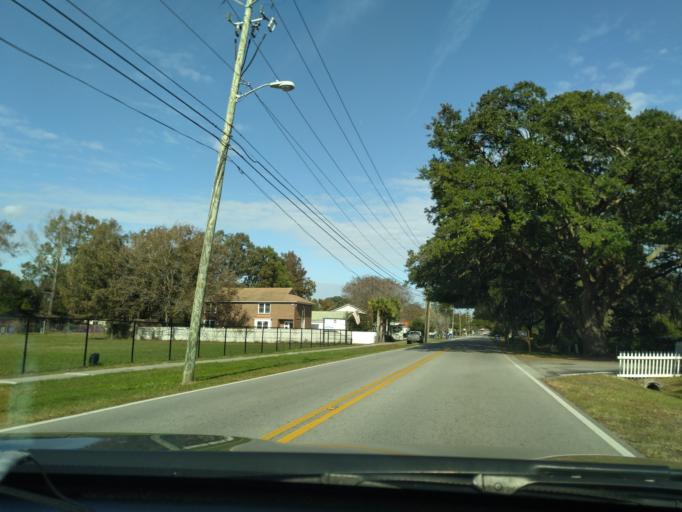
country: US
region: South Carolina
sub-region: Charleston County
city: North Charleston
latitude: 32.7916
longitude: -80.0192
